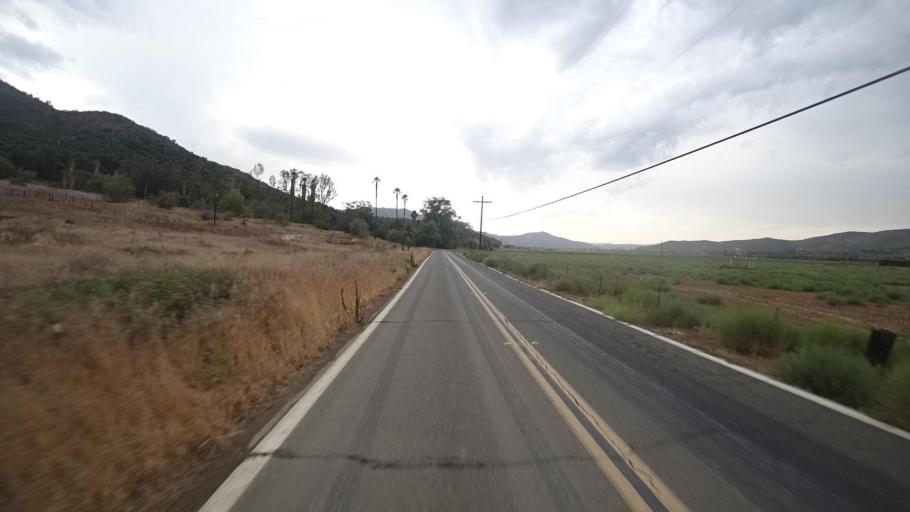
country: US
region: California
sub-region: San Diego County
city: San Pasqual
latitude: 33.0846
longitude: -116.9610
